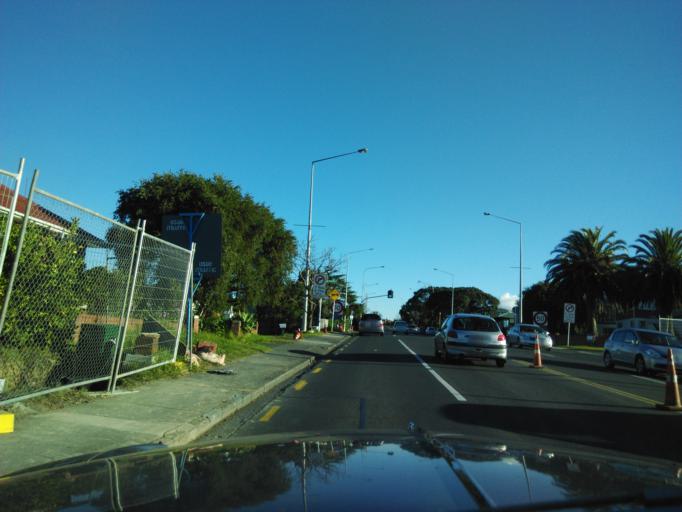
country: NZ
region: Auckland
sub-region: Auckland
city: Rosebank
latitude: -36.8594
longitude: 174.6518
